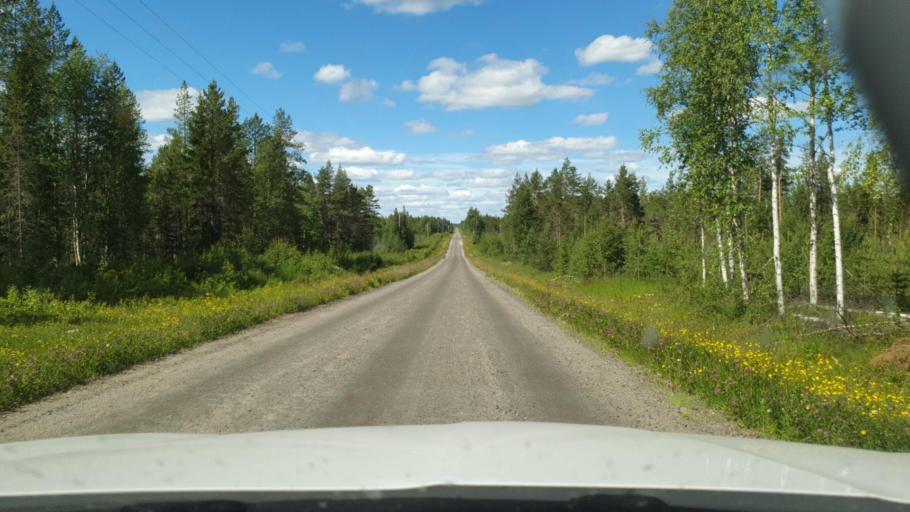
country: SE
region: Vaesterbotten
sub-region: Skelleftea Kommun
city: Backa
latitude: 65.1629
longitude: 21.1423
